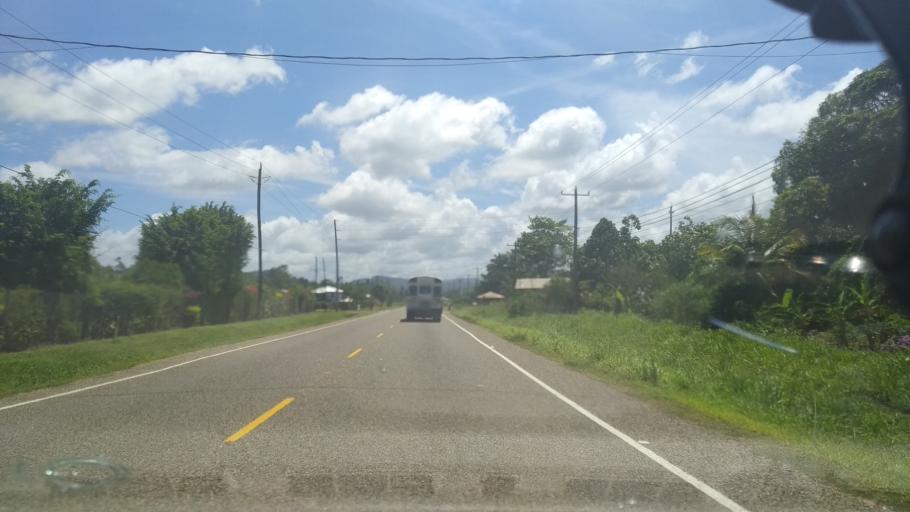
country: BZ
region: Stann Creek
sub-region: Dangriga
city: Dangriga
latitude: 17.0019
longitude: -88.3093
